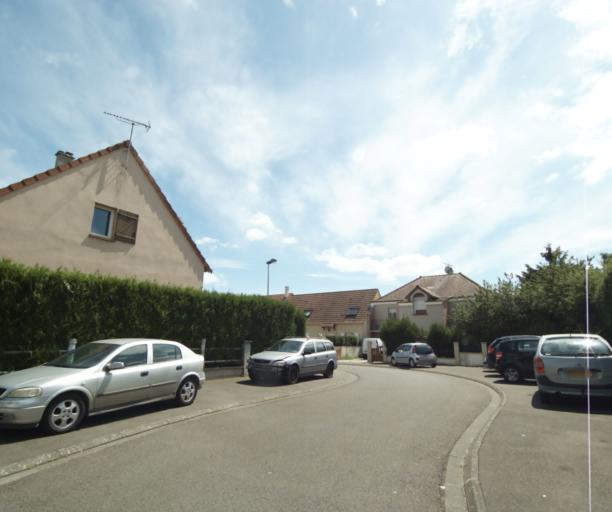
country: FR
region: Centre
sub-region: Departement d'Eure-et-Loir
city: Luce
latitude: 48.4377
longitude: 1.4676
